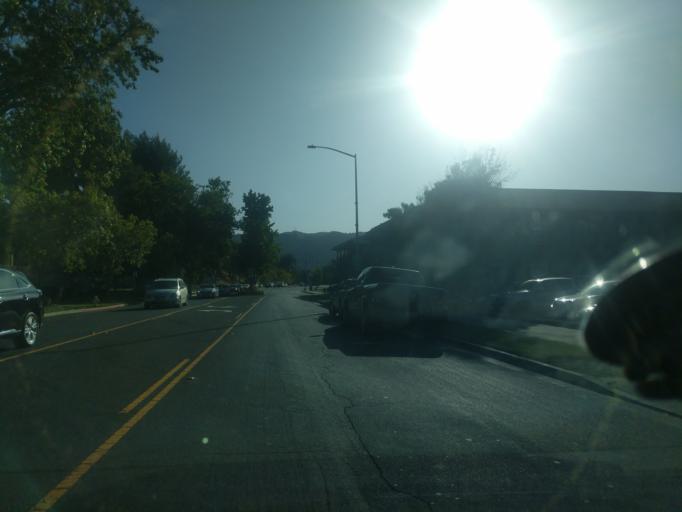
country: US
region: California
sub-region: Alameda County
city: Pleasanton
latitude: 37.6574
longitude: -121.8764
